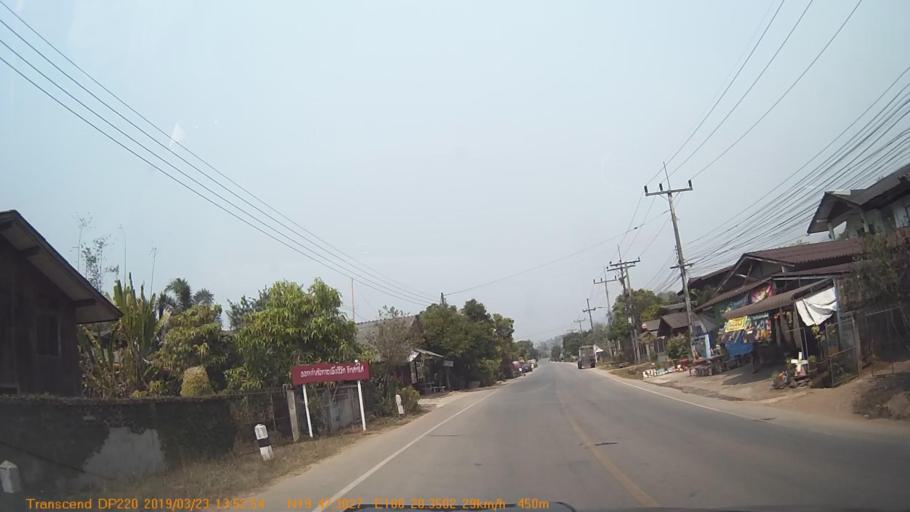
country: TH
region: Chiang Rai
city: Khun Tan
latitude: 19.7886
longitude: 100.3393
